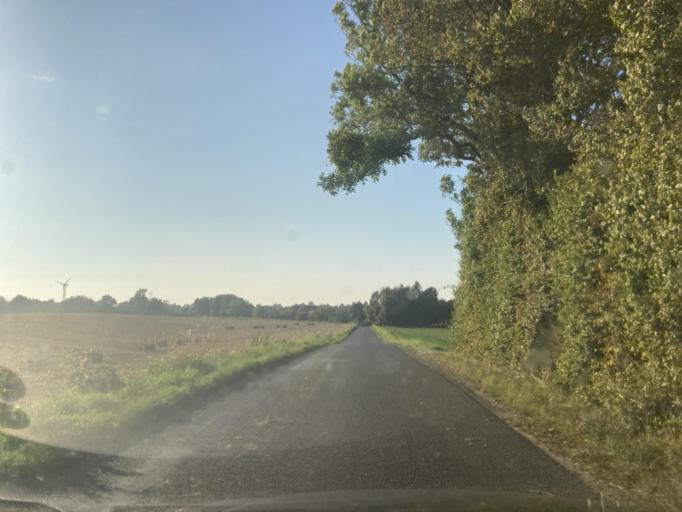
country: DK
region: South Denmark
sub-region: Svendborg Kommune
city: Thuro By
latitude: 55.1132
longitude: 10.7369
